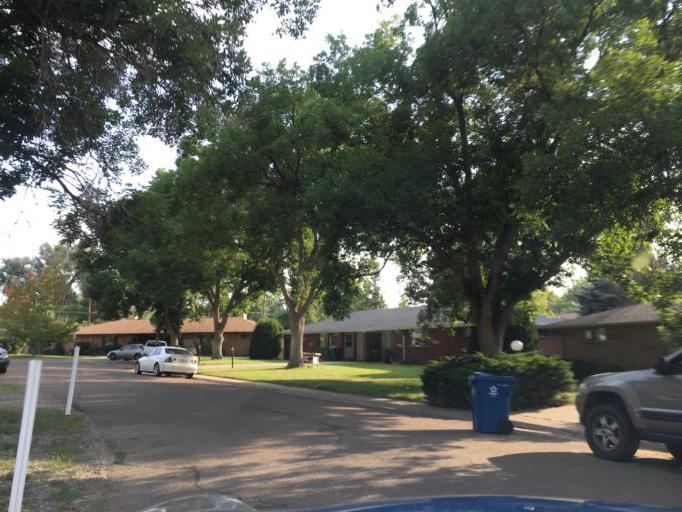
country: US
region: Colorado
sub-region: Jefferson County
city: Wheat Ridge
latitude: 39.7459
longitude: -105.1060
